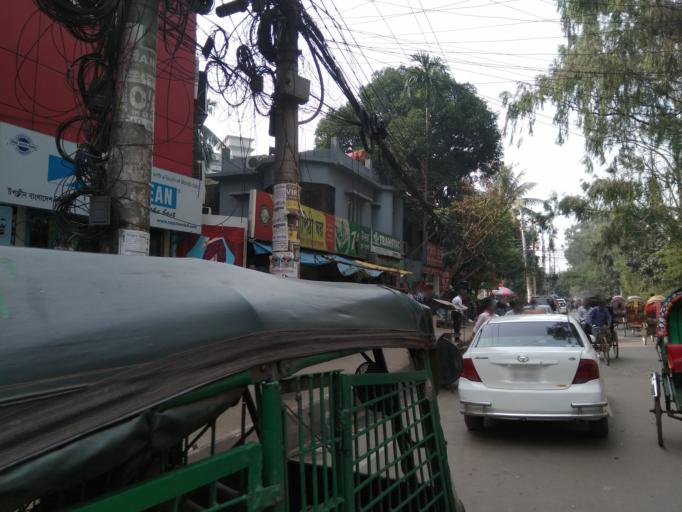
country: BD
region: Dhaka
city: Tungi
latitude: 23.8606
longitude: 90.3996
